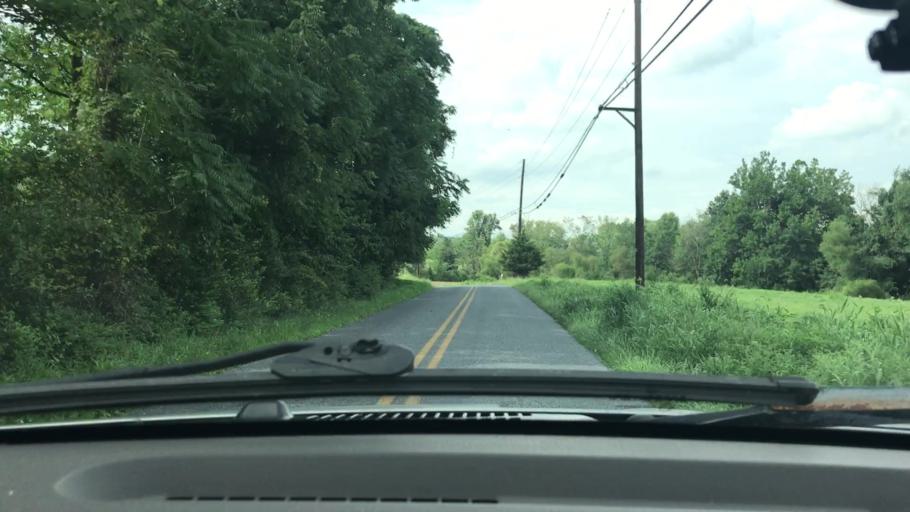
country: US
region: Pennsylvania
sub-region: Lancaster County
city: Elizabethtown
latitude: 40.1712
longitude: -76.6197
